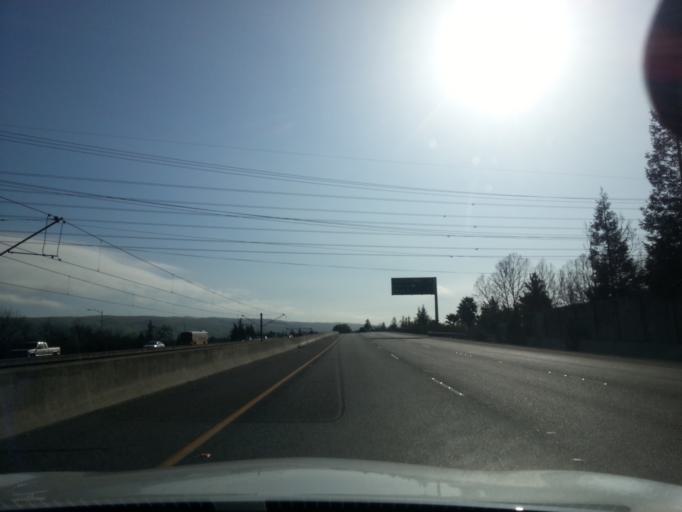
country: US
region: California
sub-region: Santa Clara County
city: Seven Trees
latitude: 37.2404
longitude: -121.7948
